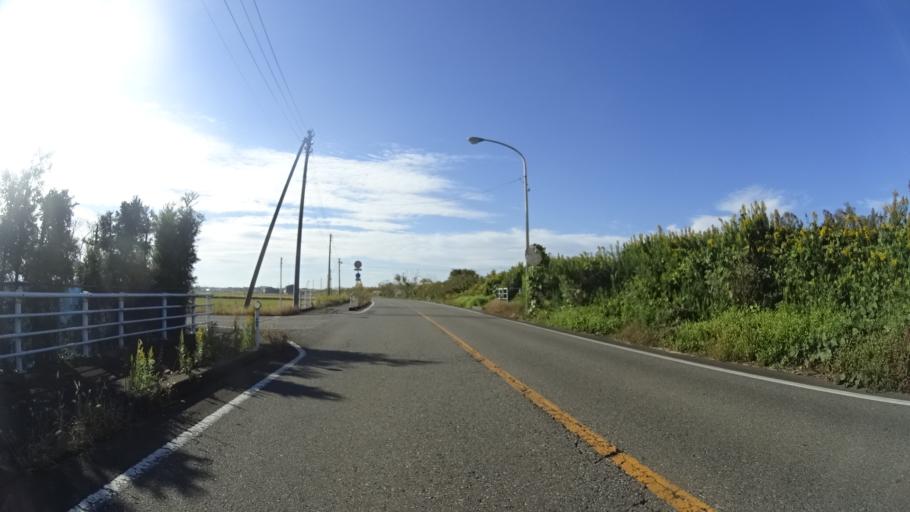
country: JP
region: Niigata
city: Yoshida-kasugacho
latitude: 37.5881
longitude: 138.8360
